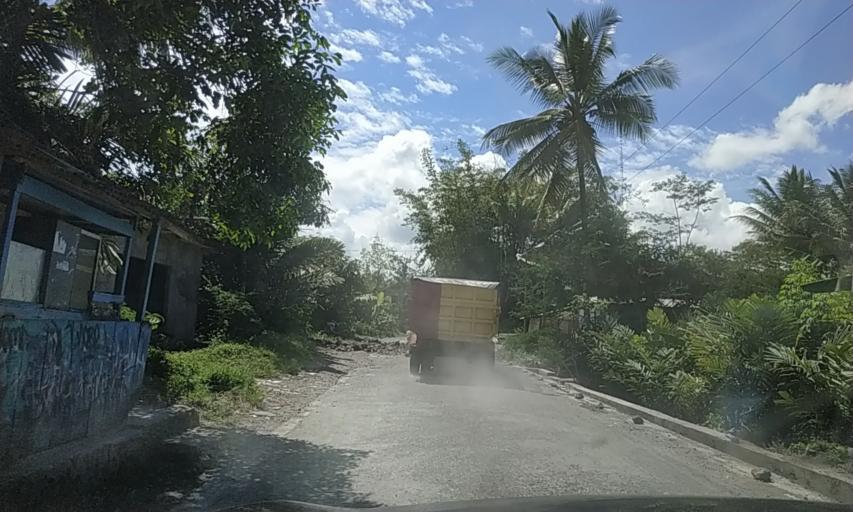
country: ID
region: Central Java
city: Muntilan
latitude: -7.6052
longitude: 110.3622
